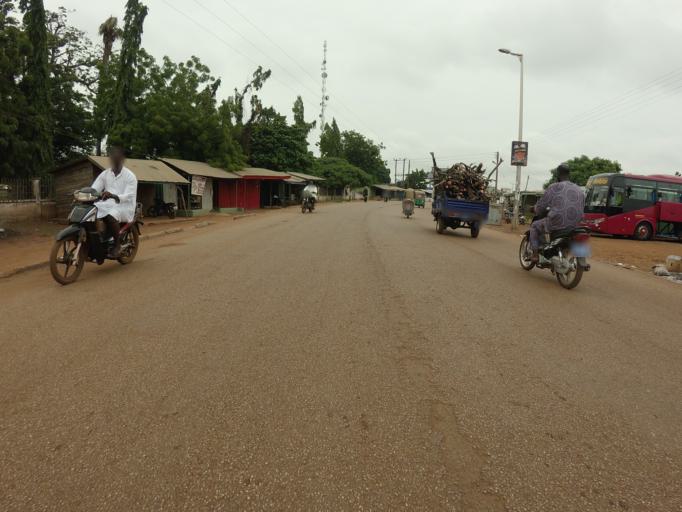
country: GH
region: Northern
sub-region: Yendi
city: Yendi
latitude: 9.4449
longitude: -0.0062
